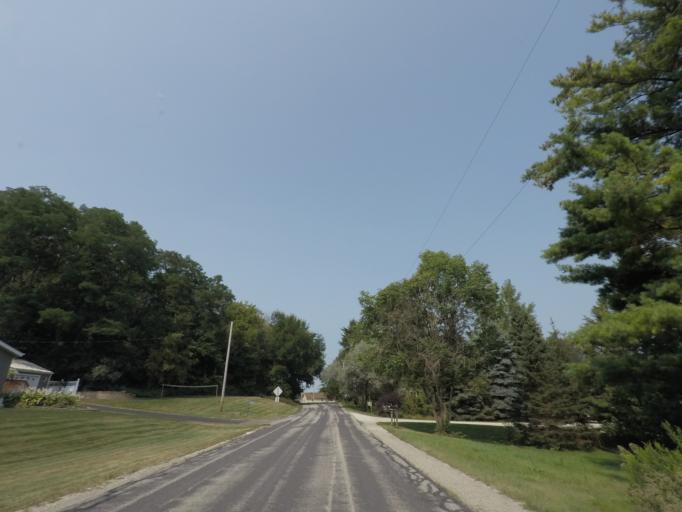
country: US
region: Wisconsin
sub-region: Jefferson County
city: Ixonia
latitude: 43.0684
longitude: -88.5953
